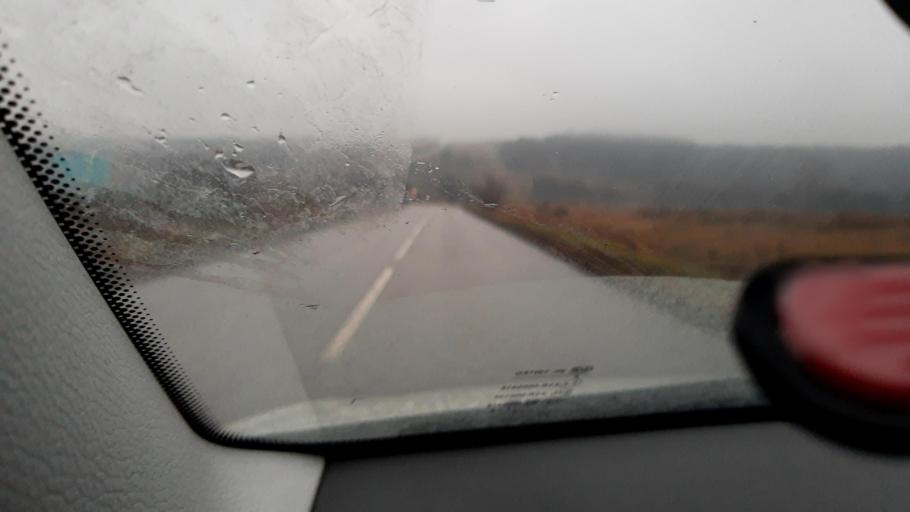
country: RU
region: Bashkortostan
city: Iglino
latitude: 54.9001
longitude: 56.2022
